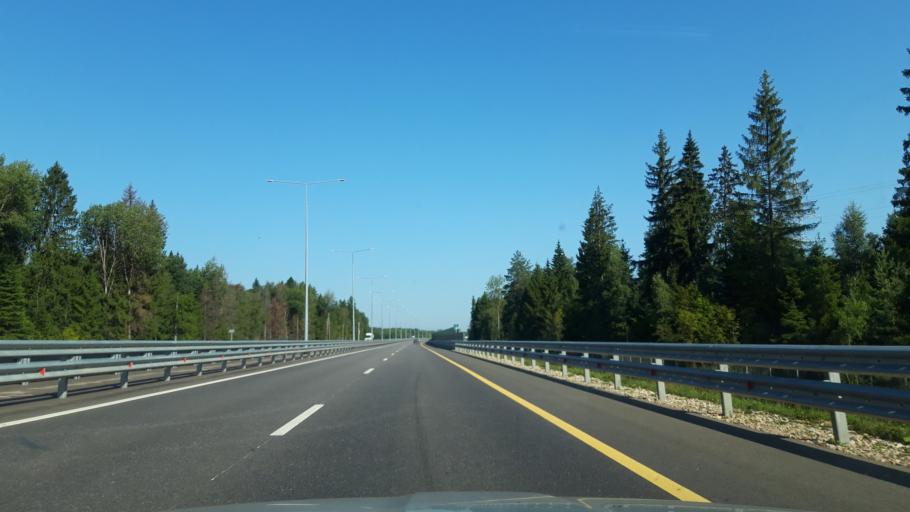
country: RU
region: Tverskaya
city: Zavidovo
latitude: 56.5091
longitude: 36.5135
